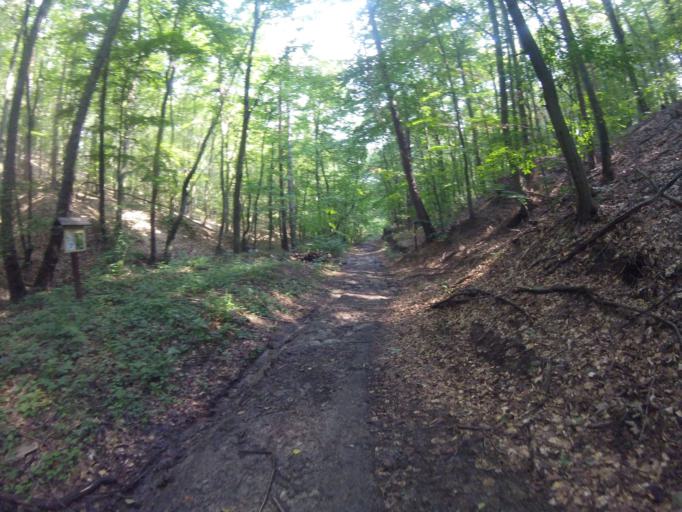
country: HU
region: Borsod-Abauj-Zemplen
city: Satoraljaujhely
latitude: 48.4549
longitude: 21.5790
